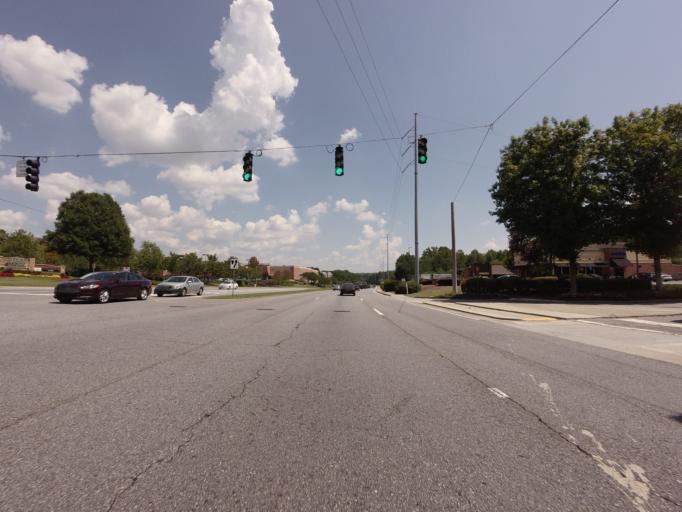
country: US
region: Georgia
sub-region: Fulton County
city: Johns Creek
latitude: 34.0143
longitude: -84.1855
